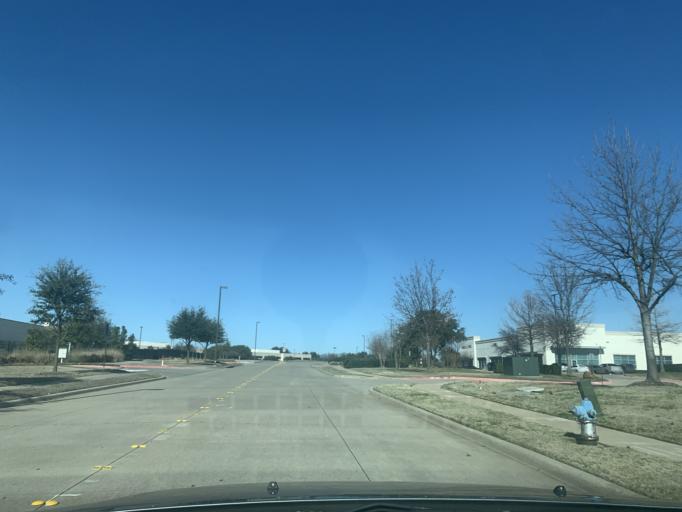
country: US
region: Texas
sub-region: Denton County
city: The Colony
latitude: 33.0653
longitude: -96.8093
